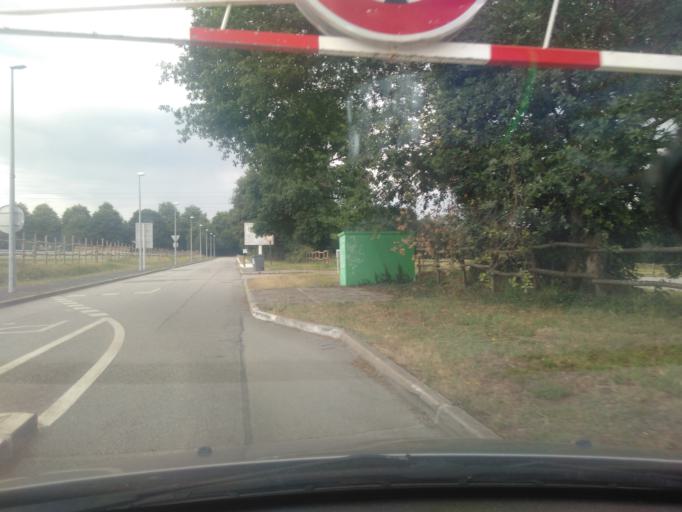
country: FR
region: Pays de la Loire
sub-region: Departement de la Vendee
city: Mouilleron-le-Captif
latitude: 46.6956
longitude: -1.4425
